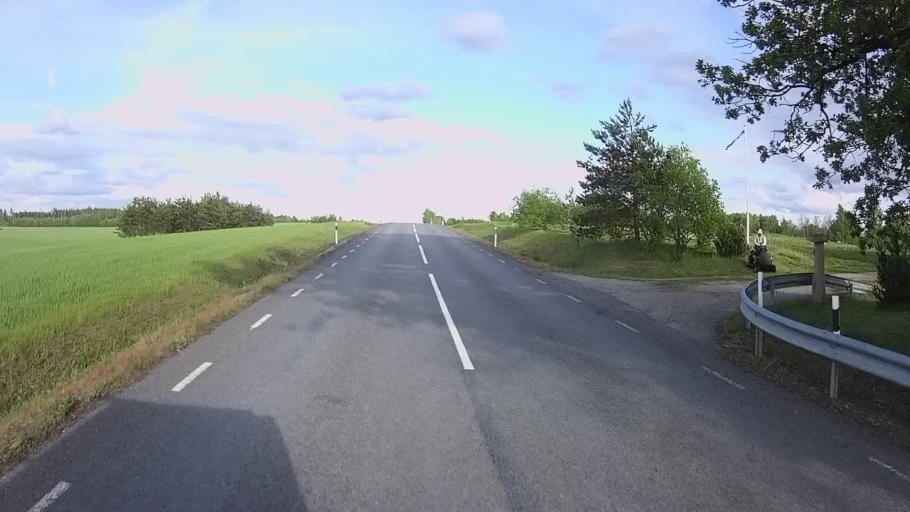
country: EE
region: Jogevamaa
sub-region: Mustvee linn
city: Mustvee
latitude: 59.0461
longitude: 27.0463
